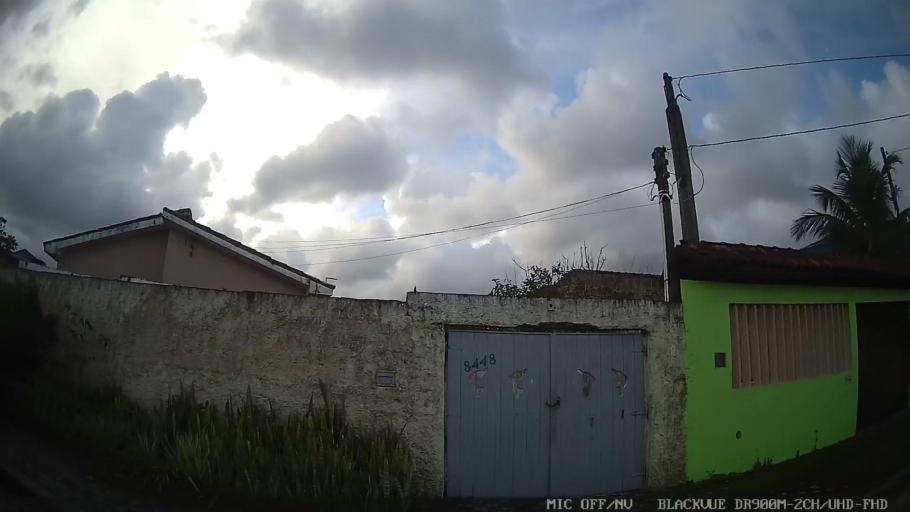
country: BR
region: Sao Paulo
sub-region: Mongagua
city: Mongagua
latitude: -24.1178
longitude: -46.6746
